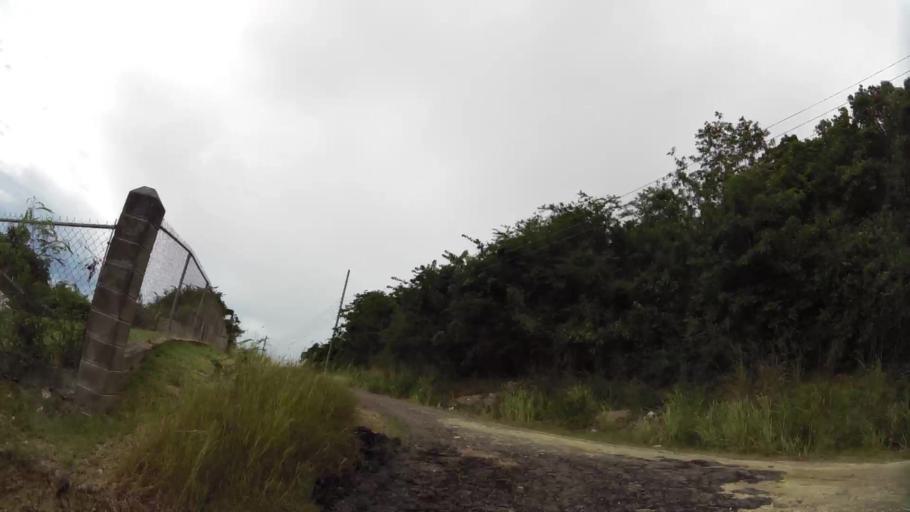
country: AG
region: Saint John
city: Potters Village
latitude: 17.0869
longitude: -61.8097
